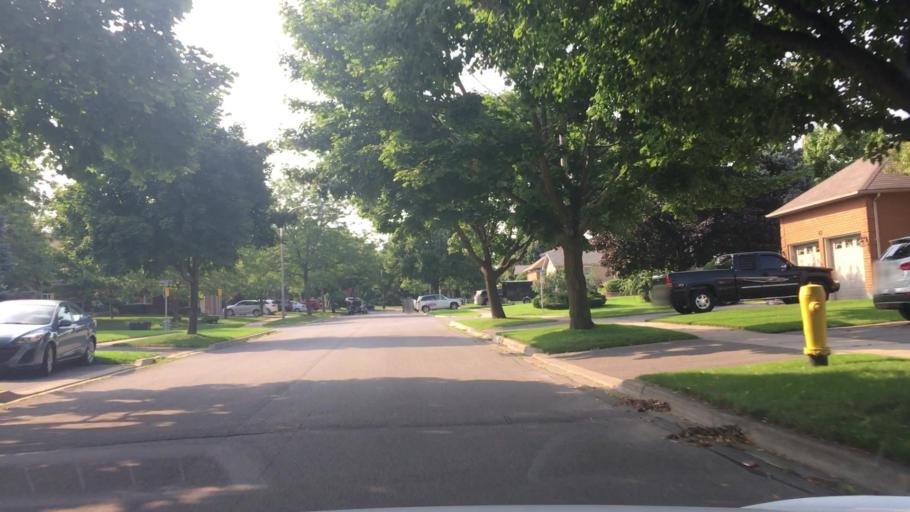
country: CA
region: Ontario
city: Ajax
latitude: 43.8791
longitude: -78.9697
